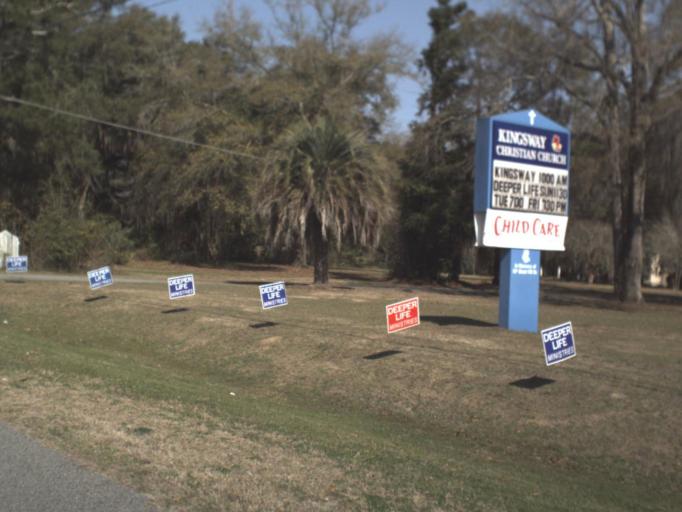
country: US
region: Florida
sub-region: Leon County
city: Tallahassee
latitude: 30.5074
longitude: -84.3343
